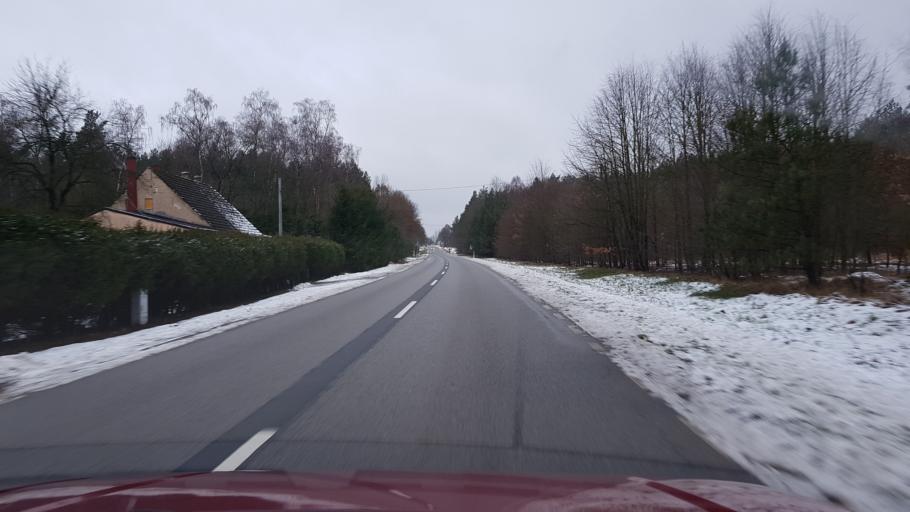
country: PL
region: West Pomeranian Voivodeship
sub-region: Powiat goleniowski
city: Nowogard
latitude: 53.6605
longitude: 15.1669
